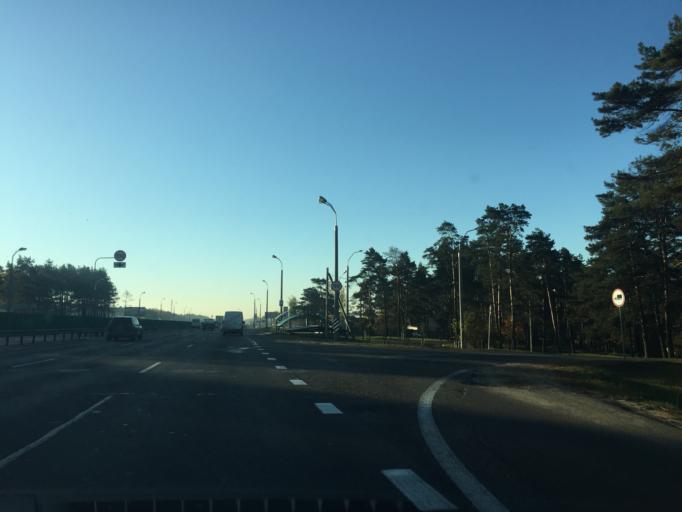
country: BY
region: Minsk
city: Vyaliki Trastsyanets
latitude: 53.9166
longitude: 27.6830
